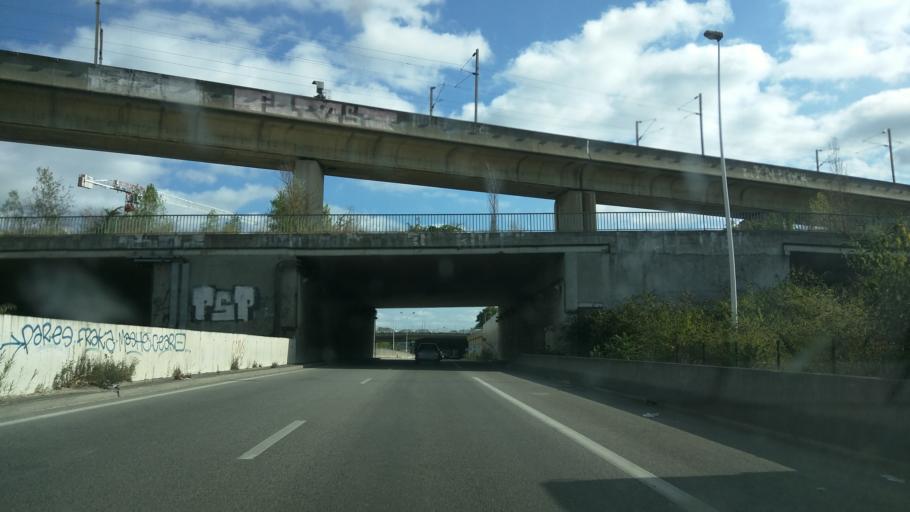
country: FR
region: Ile-de-France
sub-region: Departement des Hauts-de-Seine
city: Nanterre
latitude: 48.9019
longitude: 2.2032
